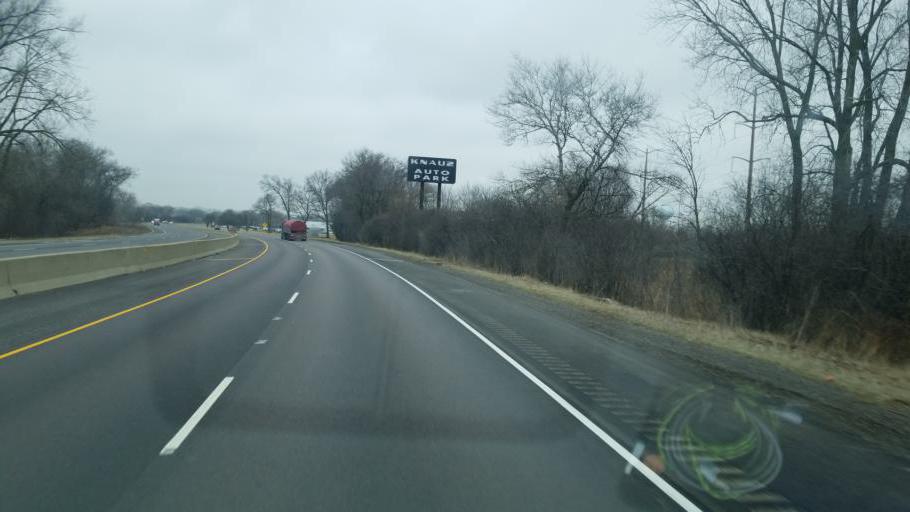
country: US
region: Illinois
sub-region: Lake County
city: Knollwood
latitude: 42.2726
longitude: -87.8657
